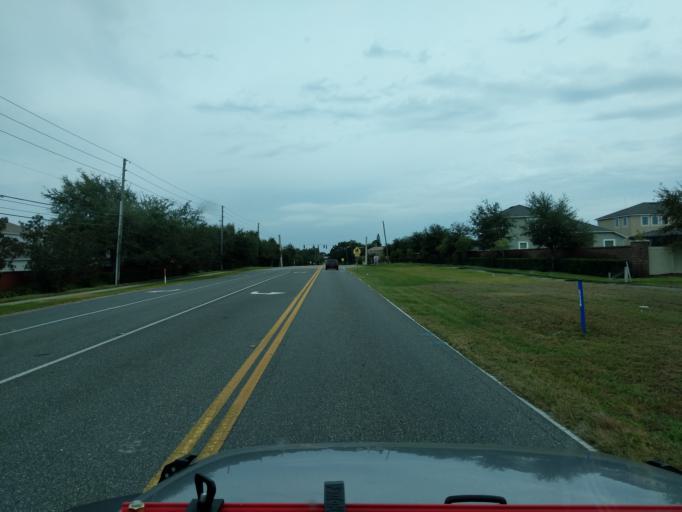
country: US
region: Florida
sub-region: Orange County
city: Oakland
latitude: 28.5367
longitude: -81.6079
